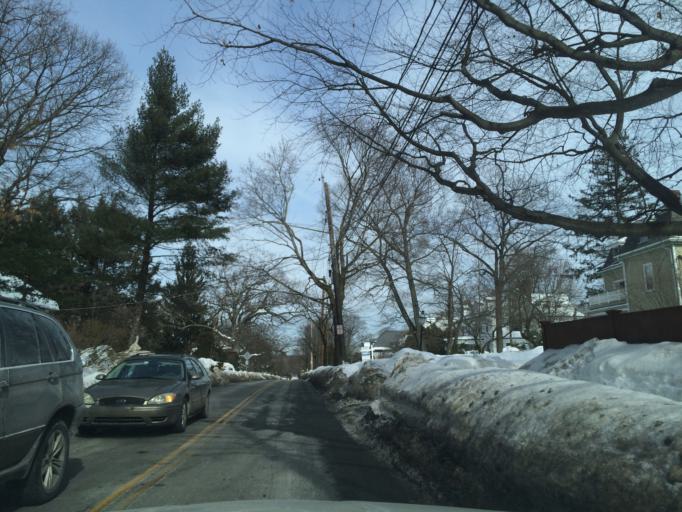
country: US
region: Massachusetts
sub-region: Middlesex County
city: Waltham
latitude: 42.3434
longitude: -71.2484
